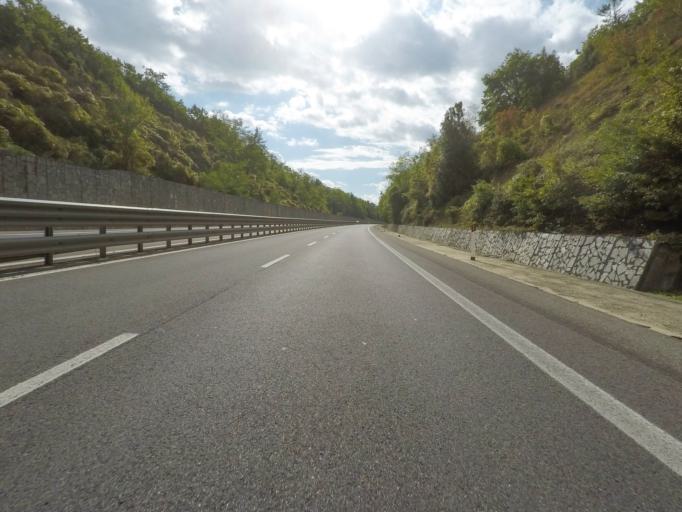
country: IT
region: Tuscany
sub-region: Provincia di Siena
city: Serre di Rapolano
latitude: 43.2815
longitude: 11.6282
